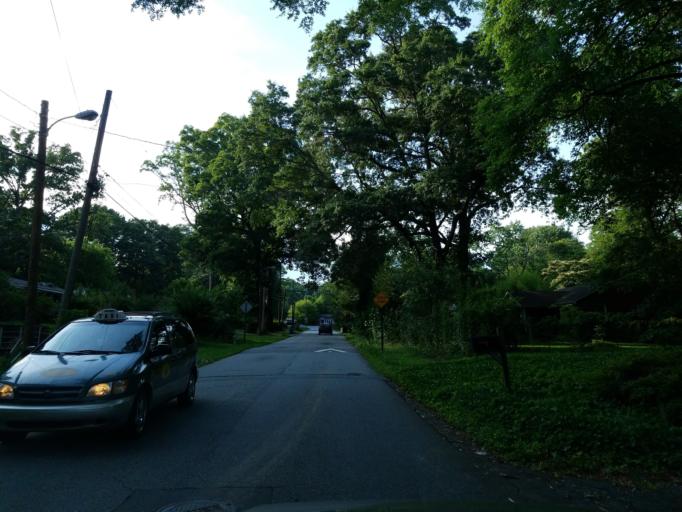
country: US
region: Georgia
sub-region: Cobb County
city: Marietta
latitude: 33.9348
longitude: -84.5491
